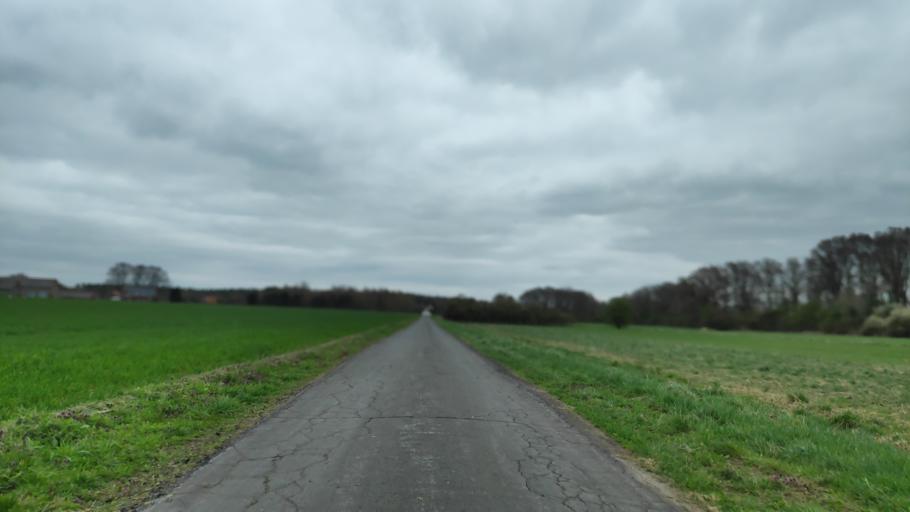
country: DE
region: North Rhine-Westphalia
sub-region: Regierungsbezirk Detmold
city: Petershagen
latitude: 52.3649
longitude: 8.8937
